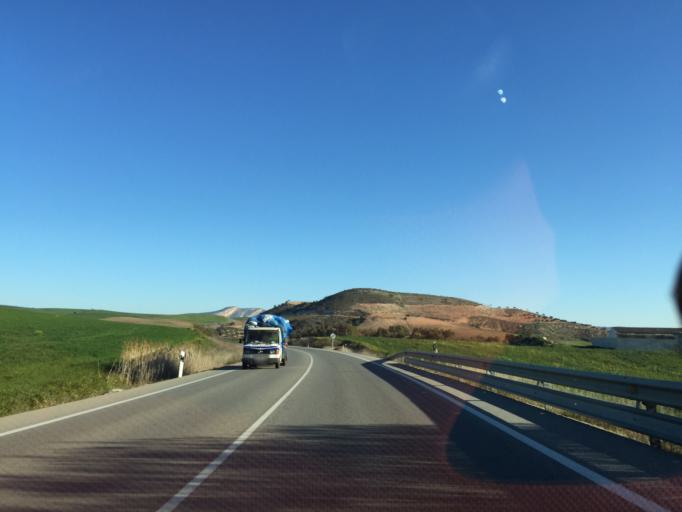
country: ES
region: Andalusia
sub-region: Provincia de Malaga
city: Ardales
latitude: 36.9026
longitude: -4.8404
